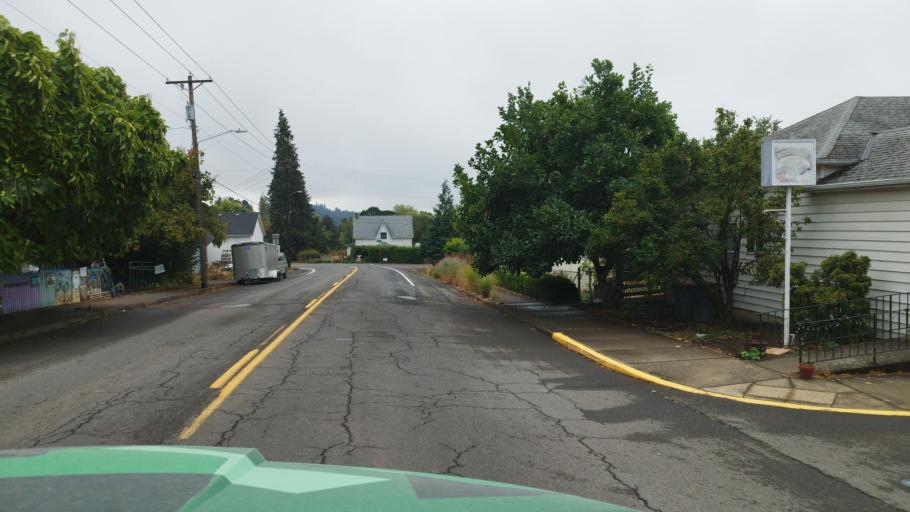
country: US
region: Oregon
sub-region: Yamhill County
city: Yamhill
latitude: 45.3400
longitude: -123.1879
